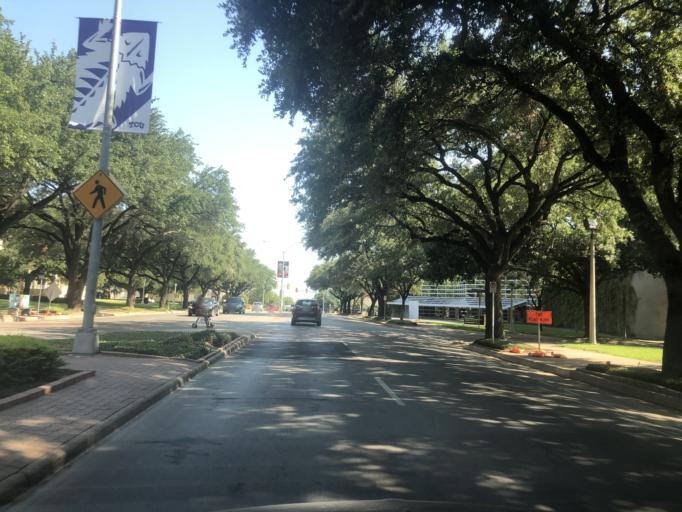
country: US
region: Texas
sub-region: Tarrant County
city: Fort Worth
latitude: 32.7103
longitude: -97.3604
